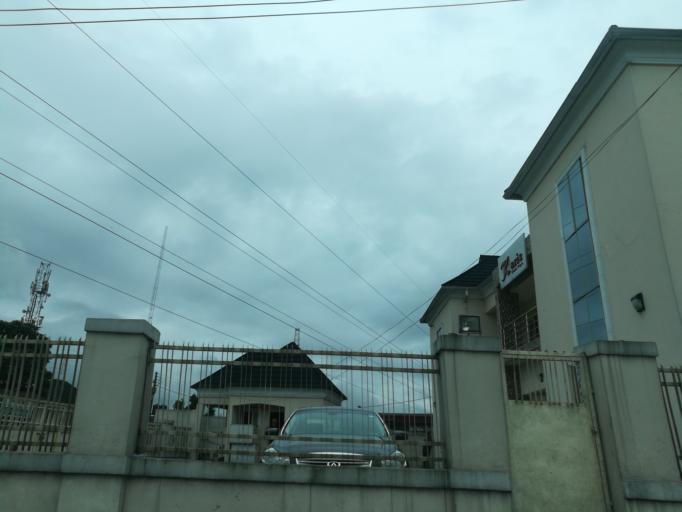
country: NG
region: Rivers
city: Port Harcourt
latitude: 4.8330
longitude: 7.0275
